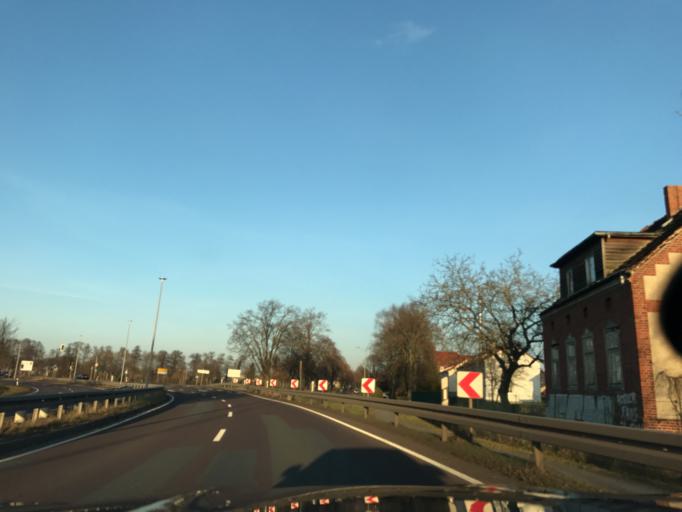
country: DE
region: Saxony-Anhalt
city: Genthin
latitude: 52.3959
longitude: 12.1433
